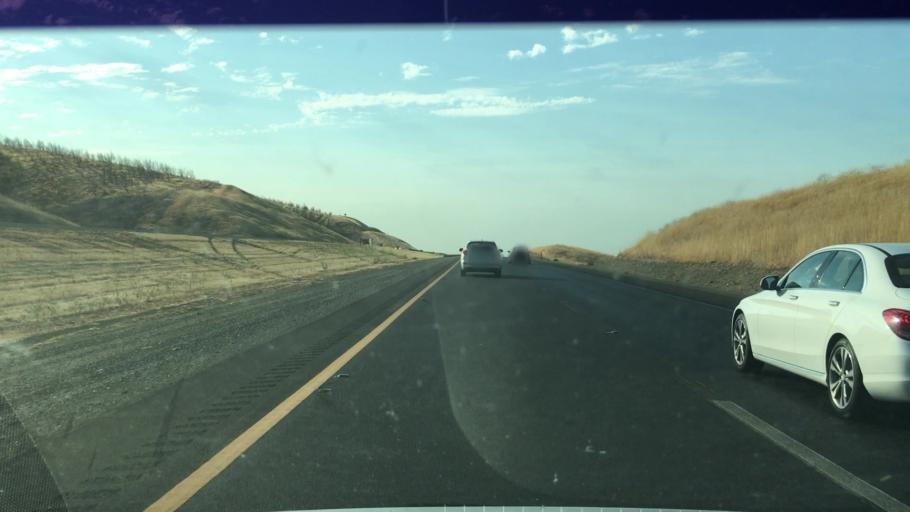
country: US
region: California
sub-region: Stanislaus County
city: Patterson
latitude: 37.4771
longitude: -121.1935
